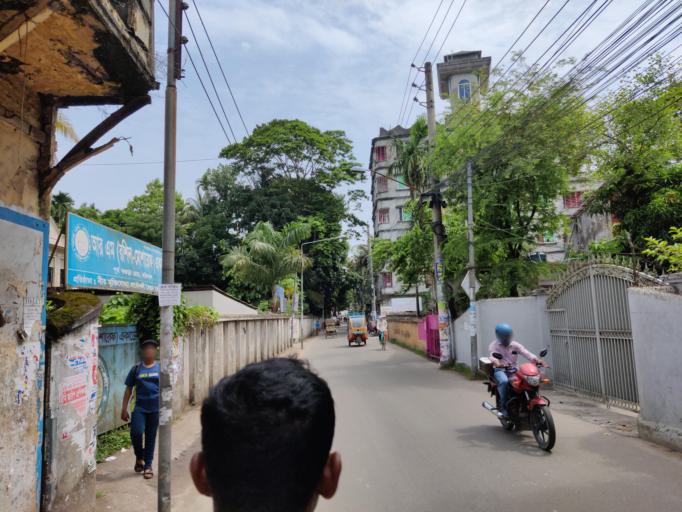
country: BD
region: Barisal
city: Barisal
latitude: 22.7031
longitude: 90.3652
